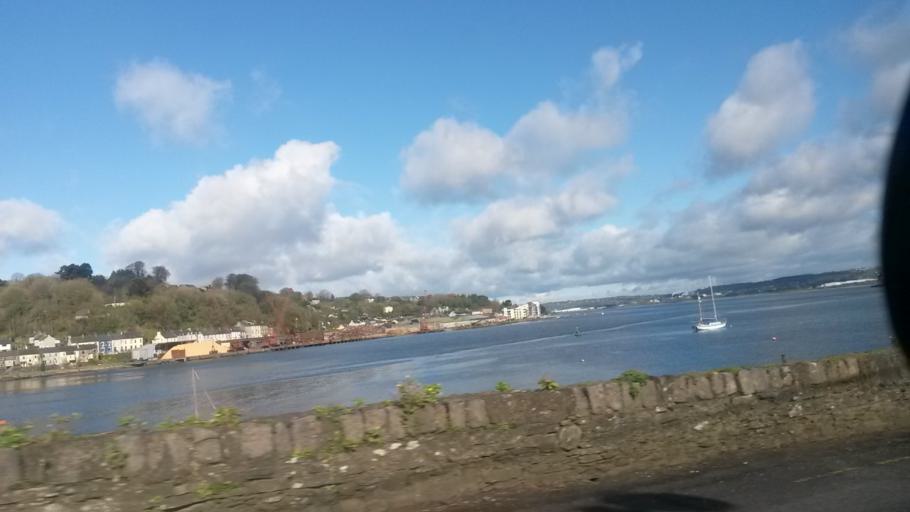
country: IE
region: Munster
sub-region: County Cork
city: Passage West
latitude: 51.8662
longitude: -8.3256
